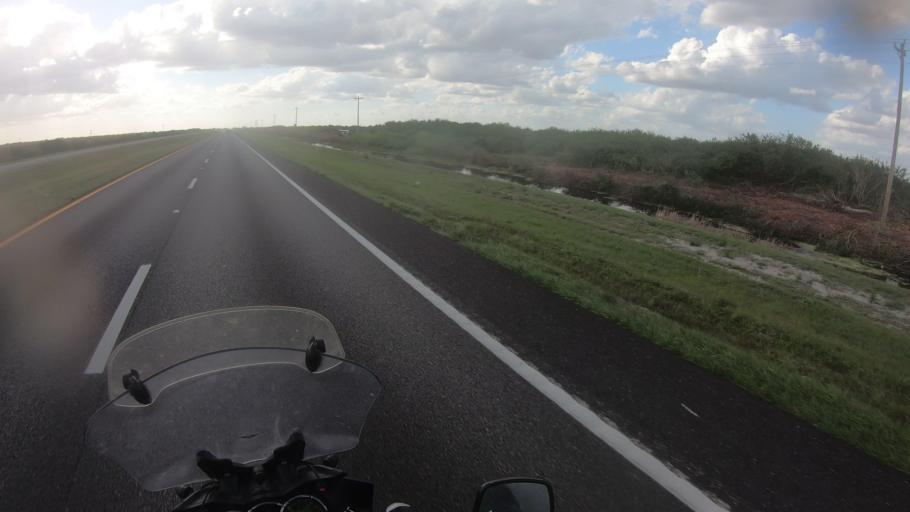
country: US
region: Florida
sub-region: Glades County
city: Moore Haven
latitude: 26.8326
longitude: -81.1665
